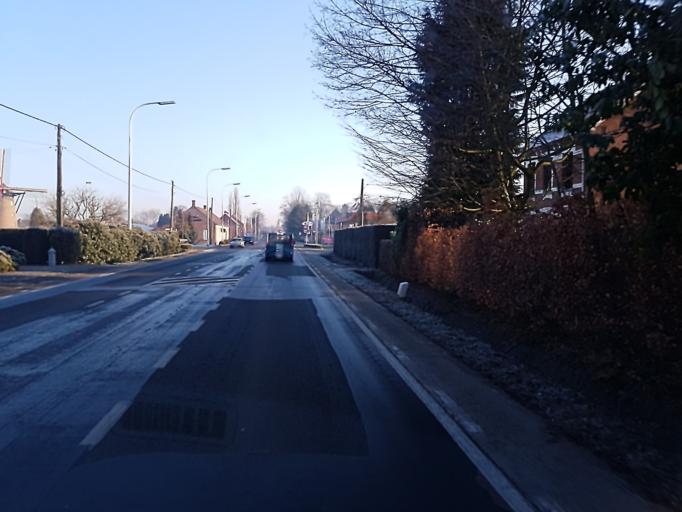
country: BE
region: Flanders
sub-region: Provincie Antwerpen
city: Zoersel
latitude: 51.2936
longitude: 4.6798
